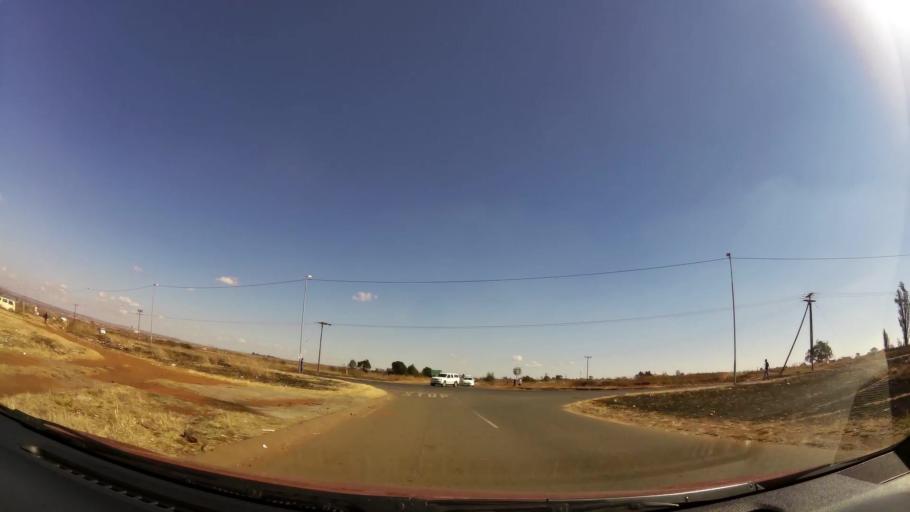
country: ZA
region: Gauteng
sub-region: City of Johannesburg Metropolitan Municipality
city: Soweto
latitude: -26.2430
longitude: 27.8048
